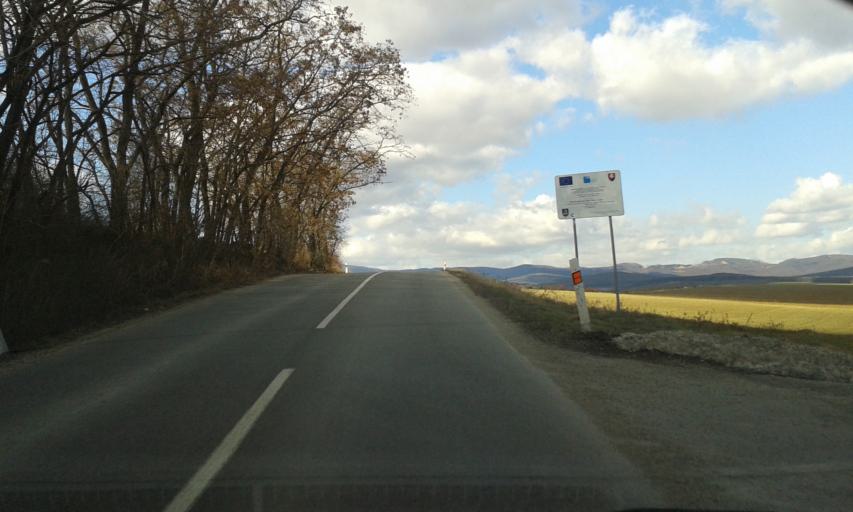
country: SK
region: Nitriansky
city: Zlate Moravce
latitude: 48.3981
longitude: 18.3491
